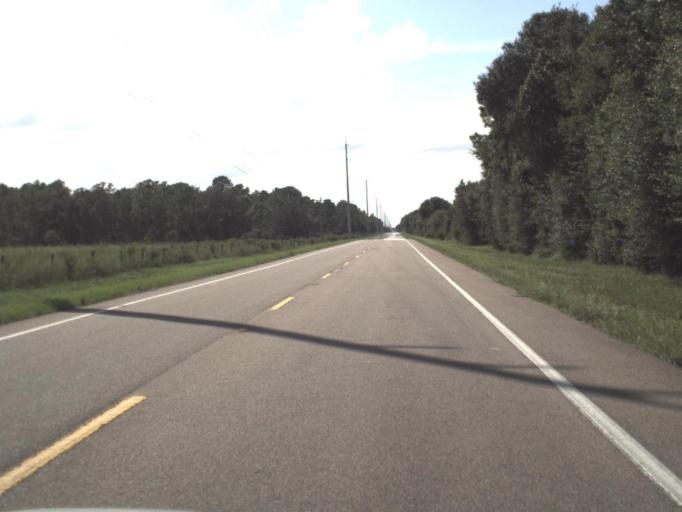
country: US
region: Florida
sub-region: Hardee County
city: Wauchula
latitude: 27.4849
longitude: -81.9605
